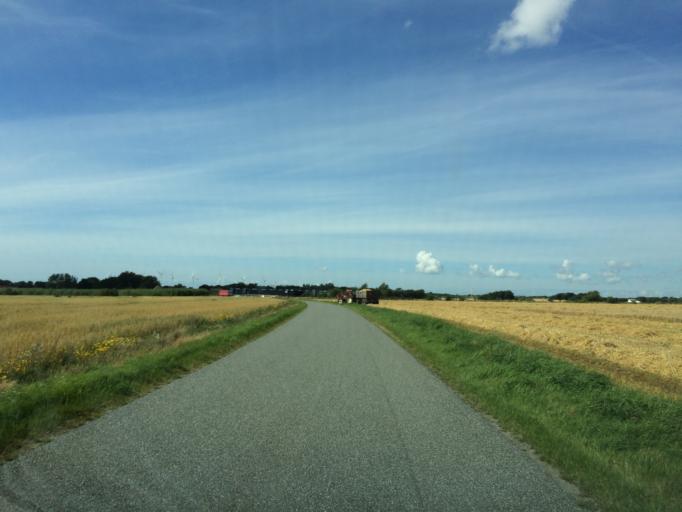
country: DK
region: Central Jutland
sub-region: Ringkobing-Skjern Kommune
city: Skjern
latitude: 56.0233
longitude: 8.4053
